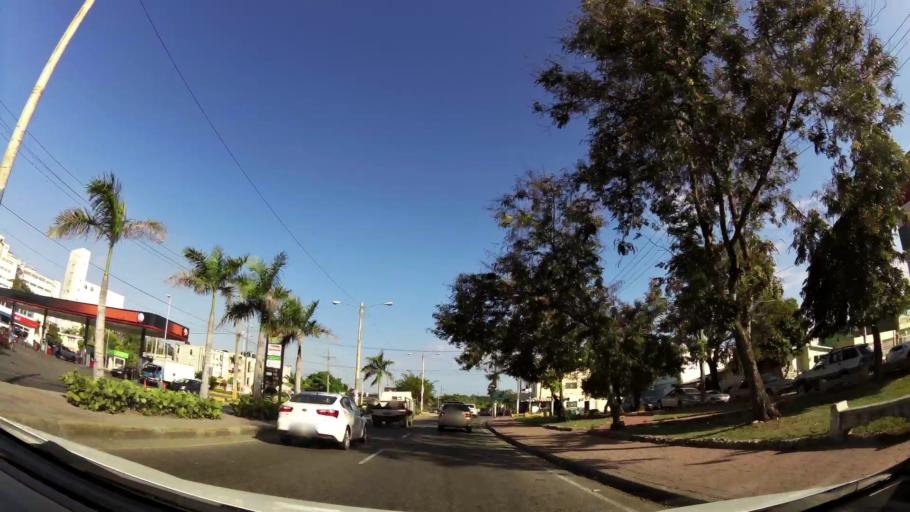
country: DO
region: Nacional
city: San Carlos
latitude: 18.4752
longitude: -69.8775
